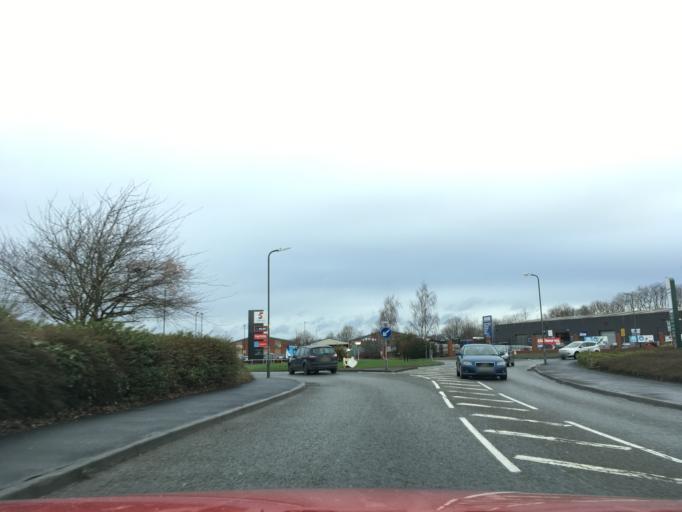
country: GB
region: England
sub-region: Worcestershire
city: Evesham
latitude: 52.0791
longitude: -1.9423
